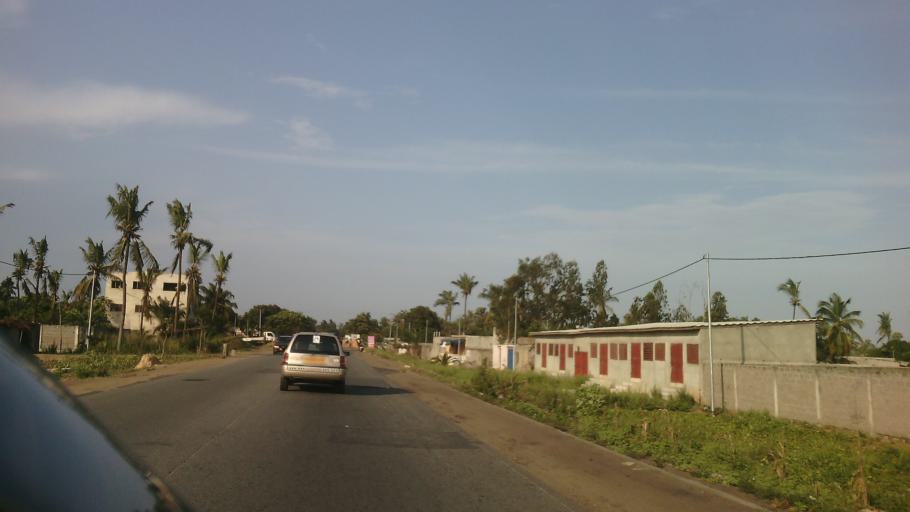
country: TG
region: Maritime
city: Vogan
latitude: 6.2013
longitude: 1.4071
